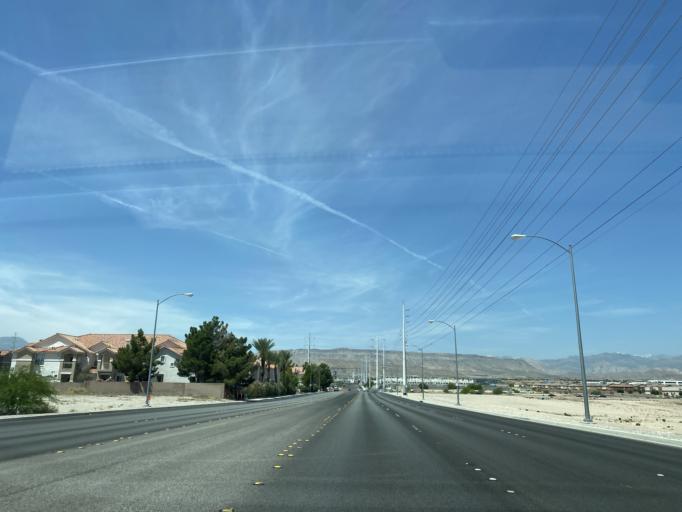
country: US
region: Nevada
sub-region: Clark County
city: Spring Valley
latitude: 36.0852
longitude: -115.2748
